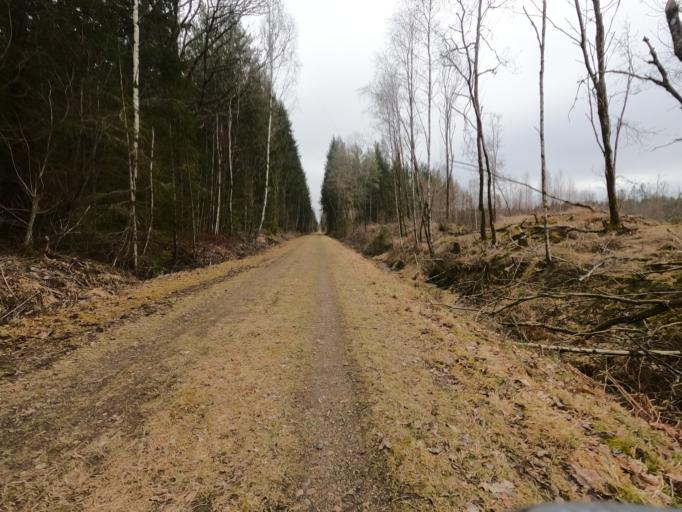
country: SE
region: Kronoberg
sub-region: Ljungby Kommun
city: Ljungby
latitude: 56.8237
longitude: 13.7330
